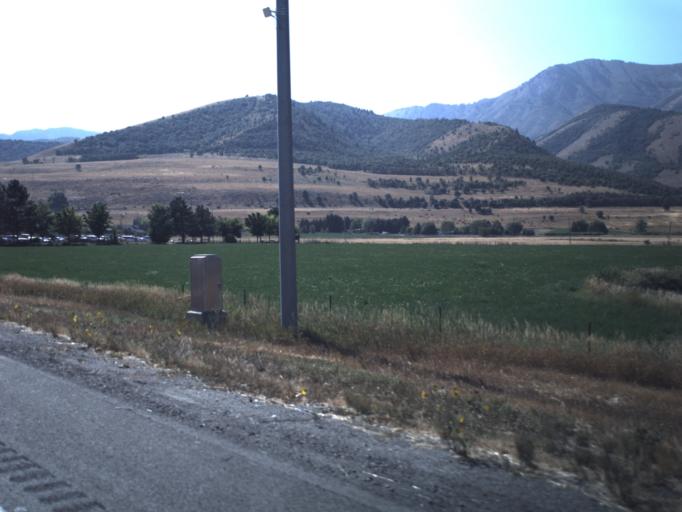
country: US
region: Utah
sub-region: Cache County
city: Wellsville
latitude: 41.6191
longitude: -111.9310
